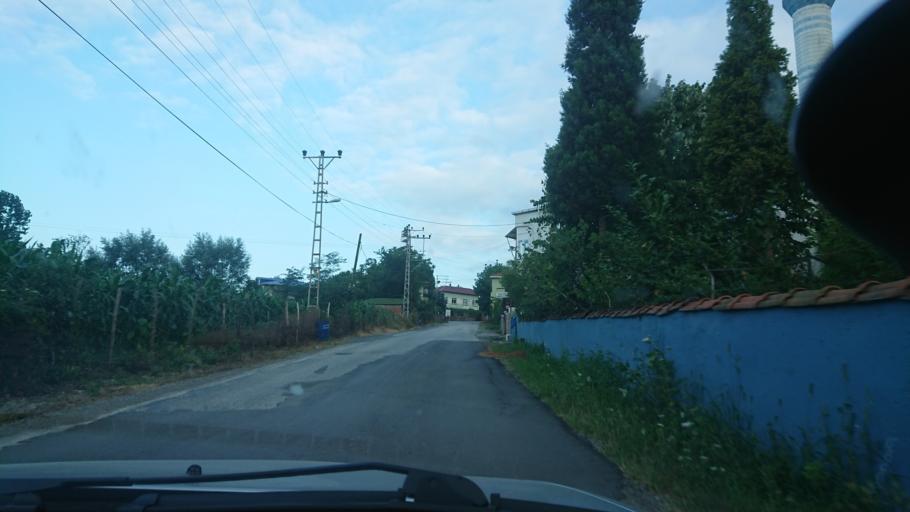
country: TR
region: Samsun
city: Tekkekoy
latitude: 41.1724
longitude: 36.5308
